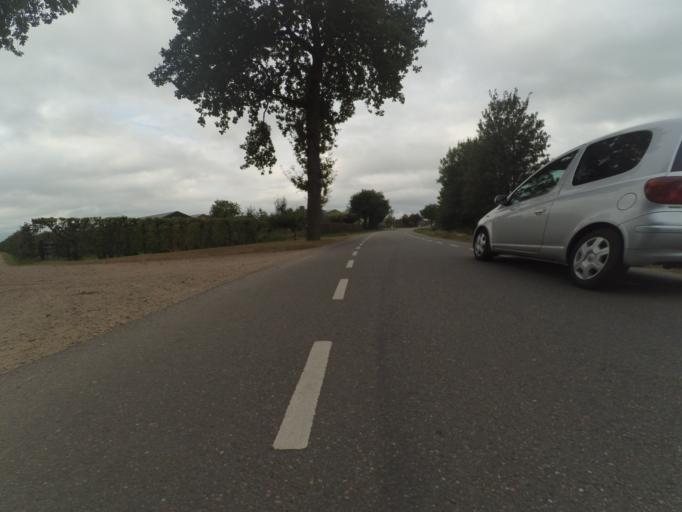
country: NL
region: Gelderland
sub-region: Gemeente Buren
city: Lienden
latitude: 51.9613
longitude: 5.4778
